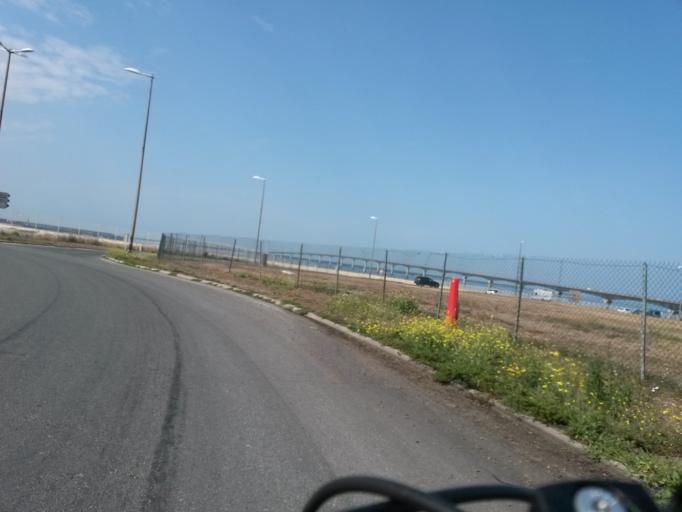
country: FR
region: Poitou-Charentes
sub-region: Departement de la Charente-Maritime
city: Rivedoux-Plage
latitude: 46.1730
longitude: -1.2180
